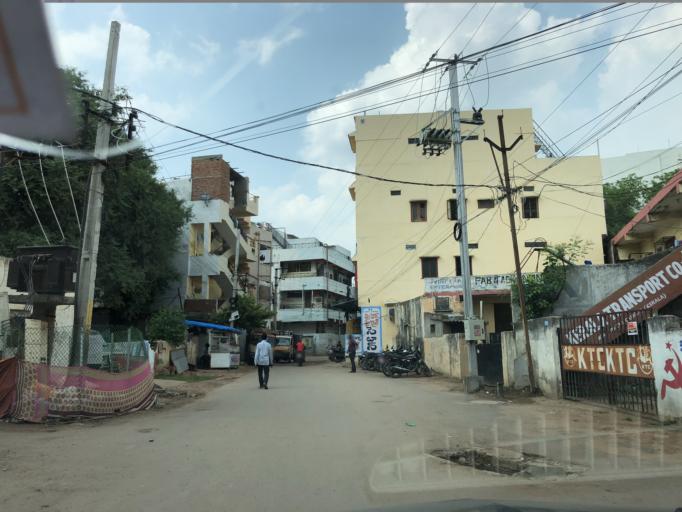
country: IN
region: Telangana
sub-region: Hyderabad
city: Malkajgiri
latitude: 17.4464
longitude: 78.4779
